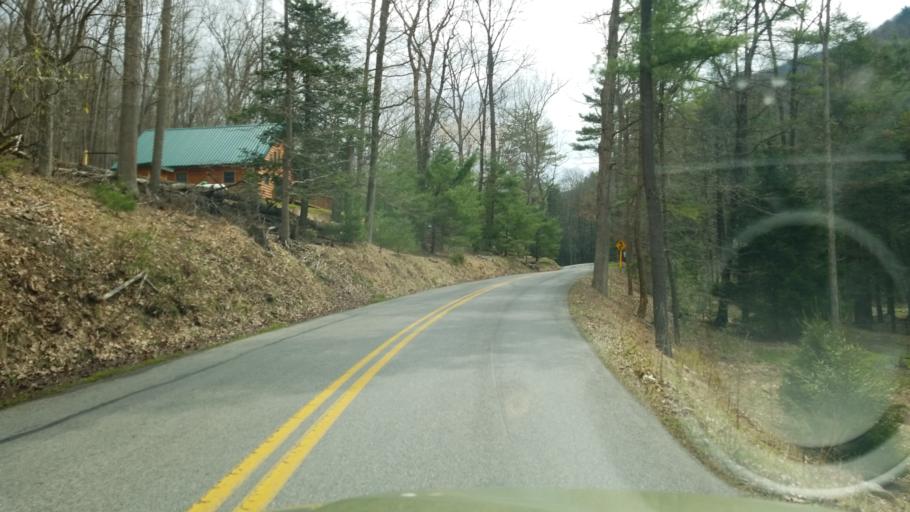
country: US
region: Pennsylvania
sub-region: Cameron County
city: Emporium
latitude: 41.2962
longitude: -78.1116
